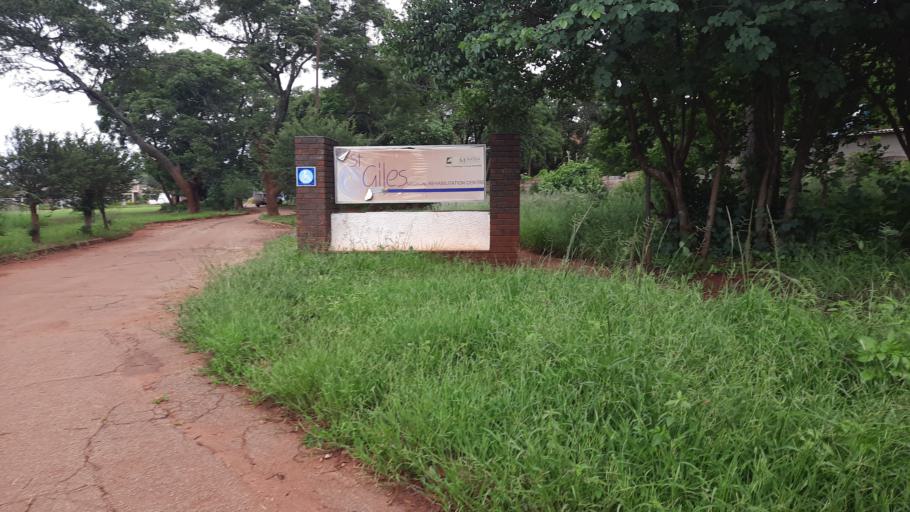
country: ZW
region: Harare
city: Harare
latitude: -17.8185
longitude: 31.0269
